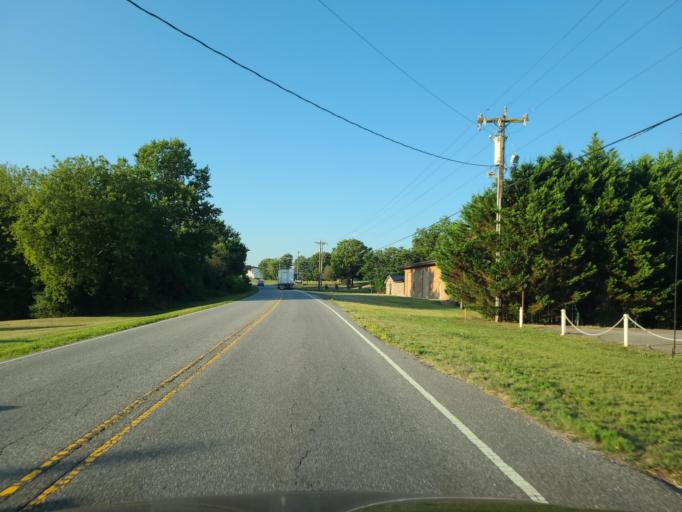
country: US
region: North Carolina
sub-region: Catawba County
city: Mountain View
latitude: 35.6391
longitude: -81.3819
